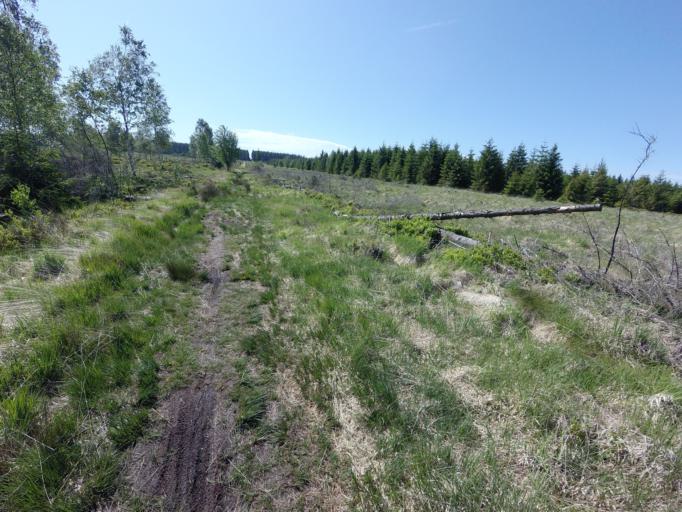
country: BE
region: Wallonia
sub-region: Province de Liege
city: Malmedy
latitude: 50.4995
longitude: 6.0321
